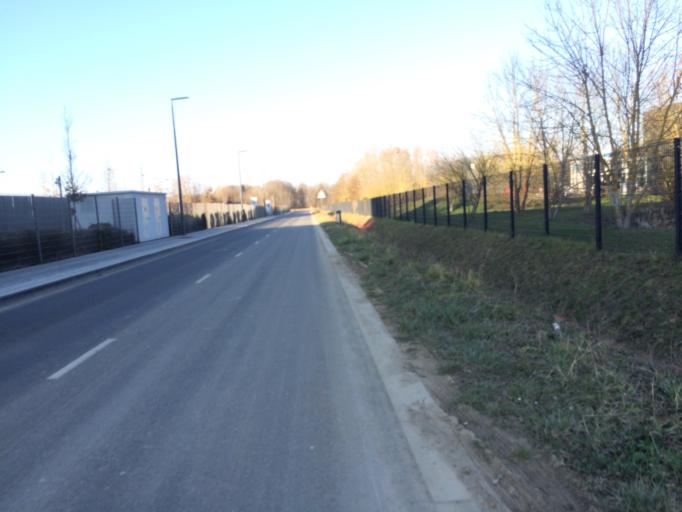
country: FR
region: Ile-de-France
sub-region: Departement de l'Essonne
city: Vauhallan
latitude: 48.7163
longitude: 2.1983
